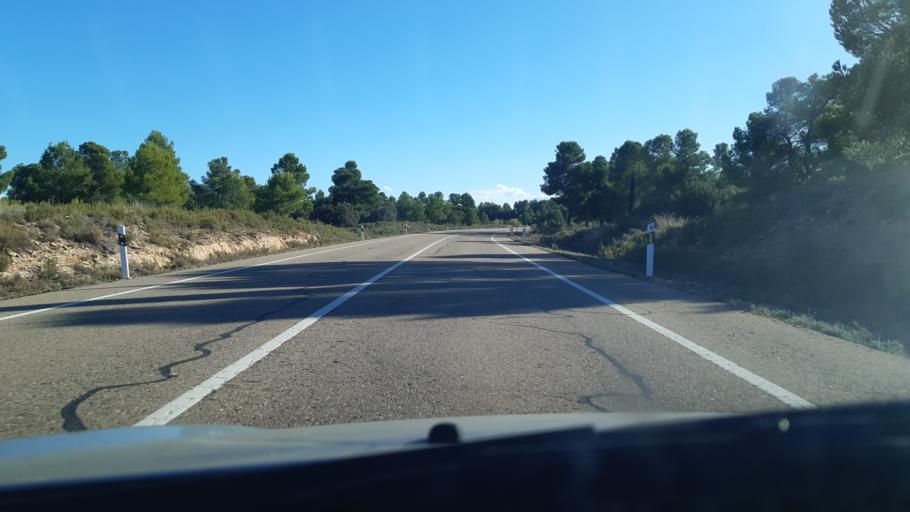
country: ES
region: Aragon
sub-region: Provincia de Teruel
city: Valjunquera
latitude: 40.9403
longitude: -0.0117
